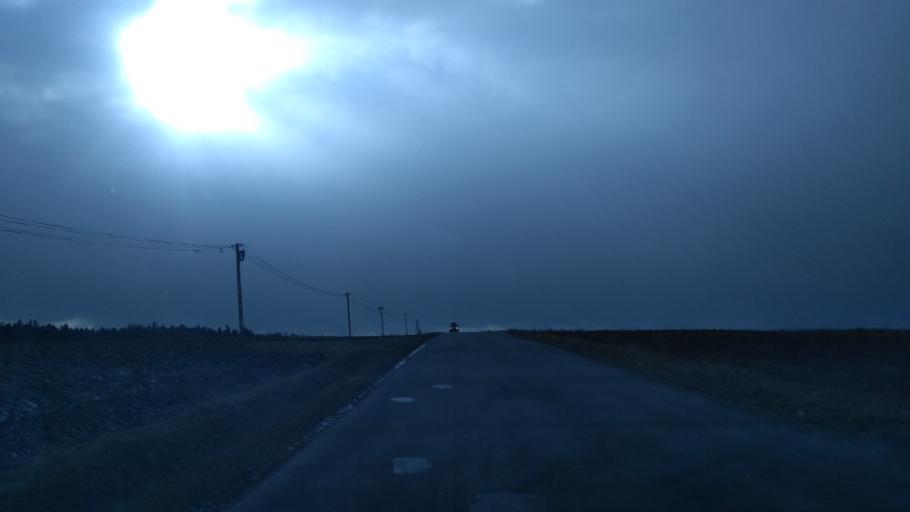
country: PL
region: Subcarpathian Voivodeship
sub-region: Powiat rzeszowski
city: Blazowa
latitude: 49.8481
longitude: 22.0873
